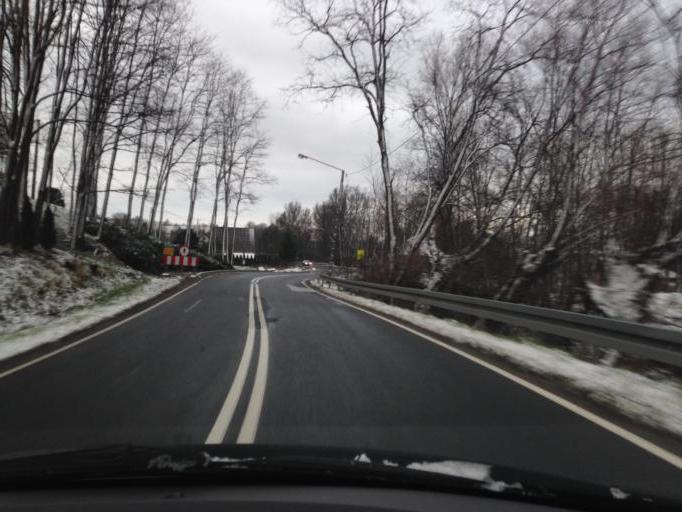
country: PL
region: Lesser Poland Voivodeship
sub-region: Powiat tarnowski
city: Rzepiennik Strzyzewski
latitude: 49.8279
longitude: 21.0047
